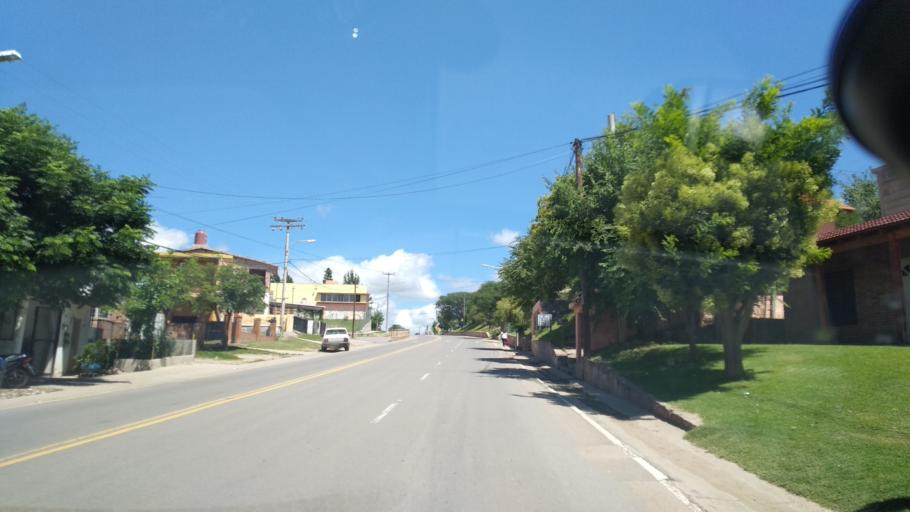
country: AR
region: Cordoba
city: Villa Cura Brochero
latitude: -31.7043
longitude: -65.0253
